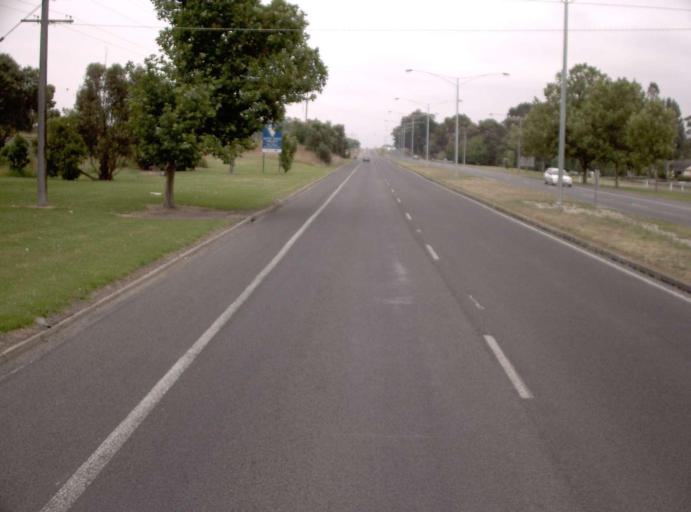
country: AU
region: Victoria
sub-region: Latrobe
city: Traralgon
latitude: -38.2044
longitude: 146.5142
